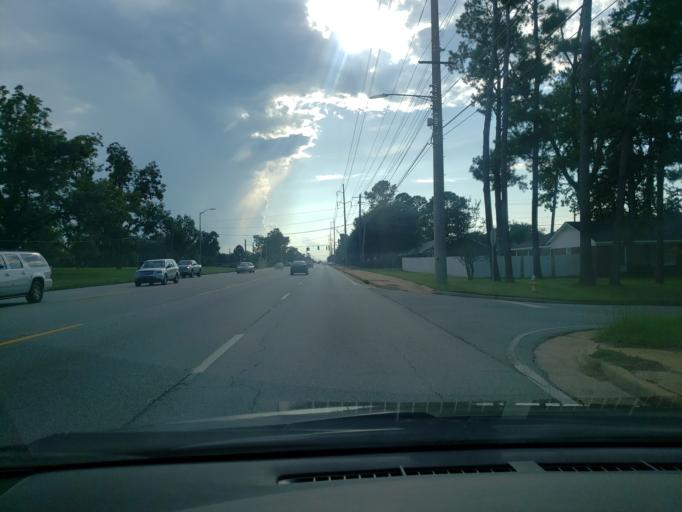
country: US
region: Georgia
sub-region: Dougherty County
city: Albany
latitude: 31.5859
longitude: -84.2124
